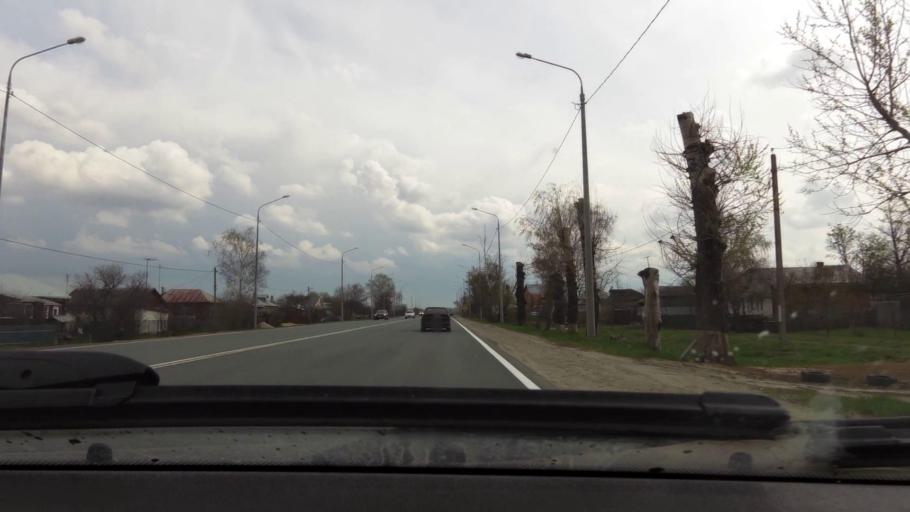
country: RU
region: Rjazan
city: Bagramovo
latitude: 54.7503
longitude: 39.4250
